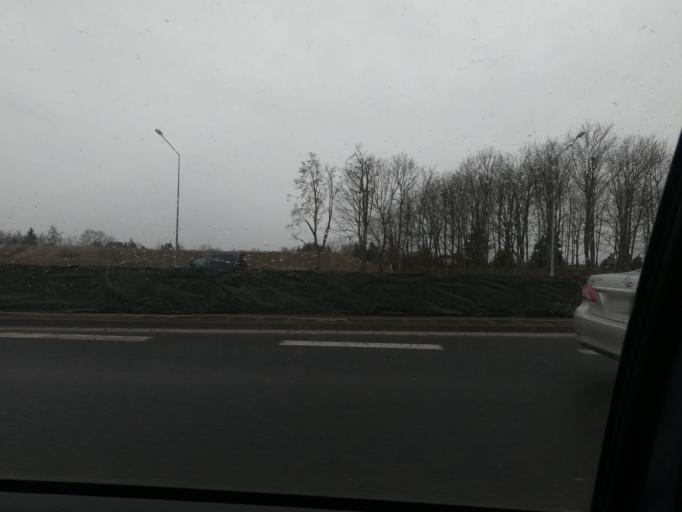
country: PL
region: Greater Poland Voivodeship
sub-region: Powiat poznanski
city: Plewiska
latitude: 52.4122
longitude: 16.8531
